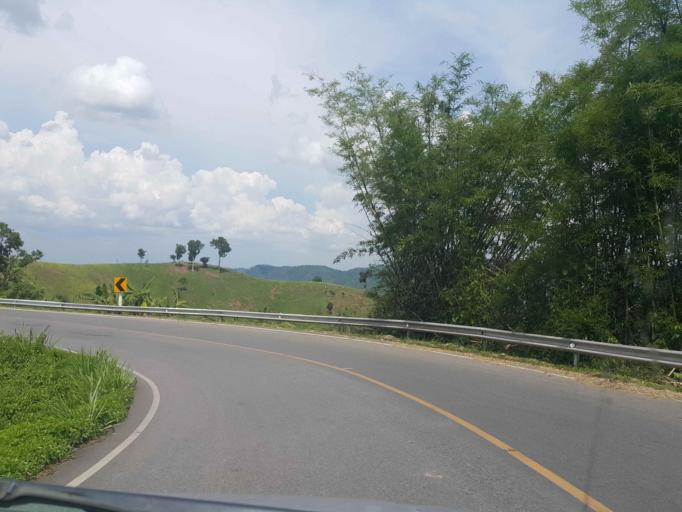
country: TH
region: Nan
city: Ban Luang
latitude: 18.8691
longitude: 100.5547
